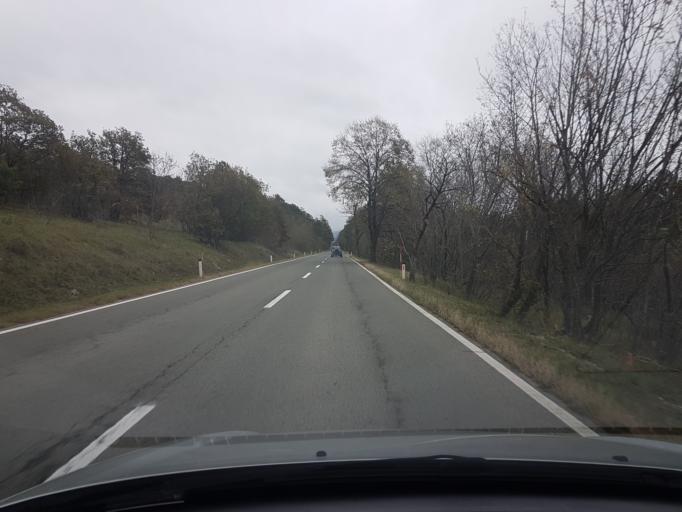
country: SI
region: Divaca
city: Divaca
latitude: 45.7309
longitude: 13.9618
